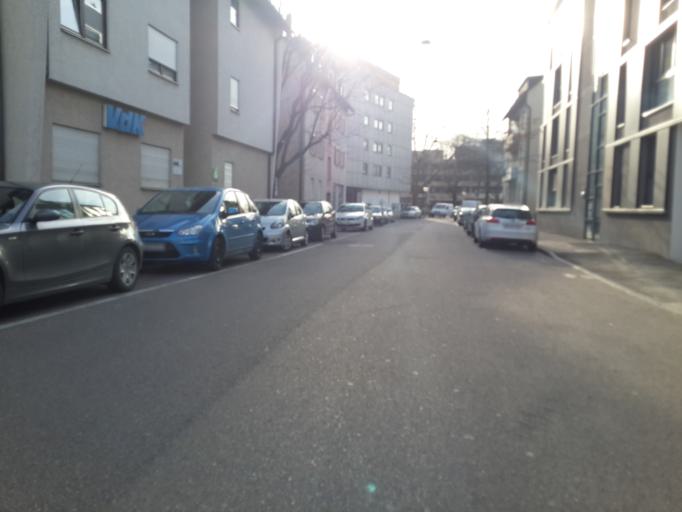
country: DE
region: Baden-Wuerttemberg
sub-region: Regierungsbezirk Stuttgart
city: Heilbronn
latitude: 49.1413
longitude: 9.2132
